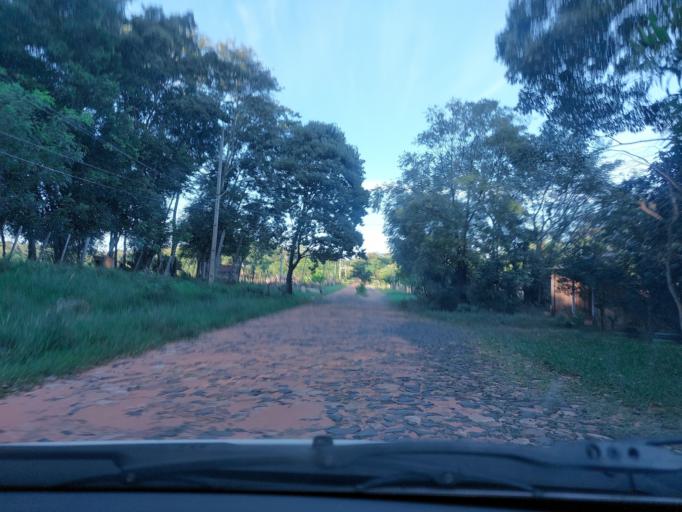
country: PY
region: San Pedro
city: Itacurubi del Rosario
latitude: -24.5623
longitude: -56.5921
